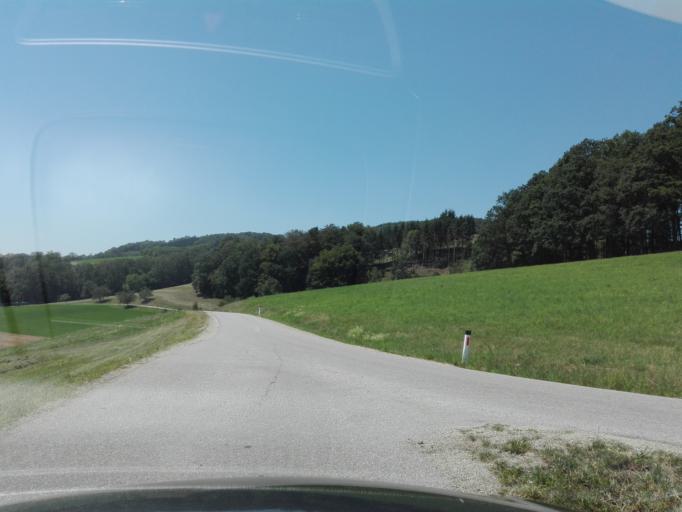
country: AT
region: Upper Austria
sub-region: Politischer Bezirk Urfahr-Umgebung
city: Engerwitzdorf
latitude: 48.2946
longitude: 14.4340
